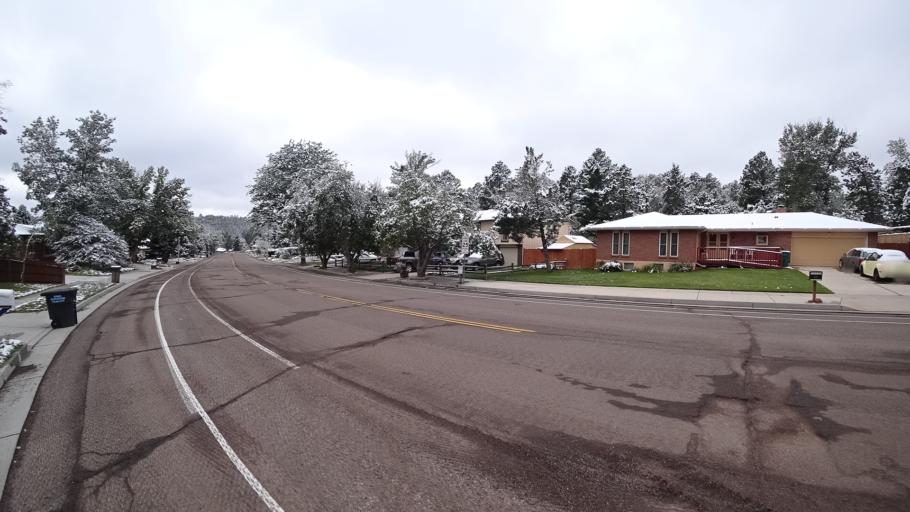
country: US
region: Colorado
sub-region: El Paso County
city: Colorado Springs
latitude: 38.8937
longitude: -104.7720
